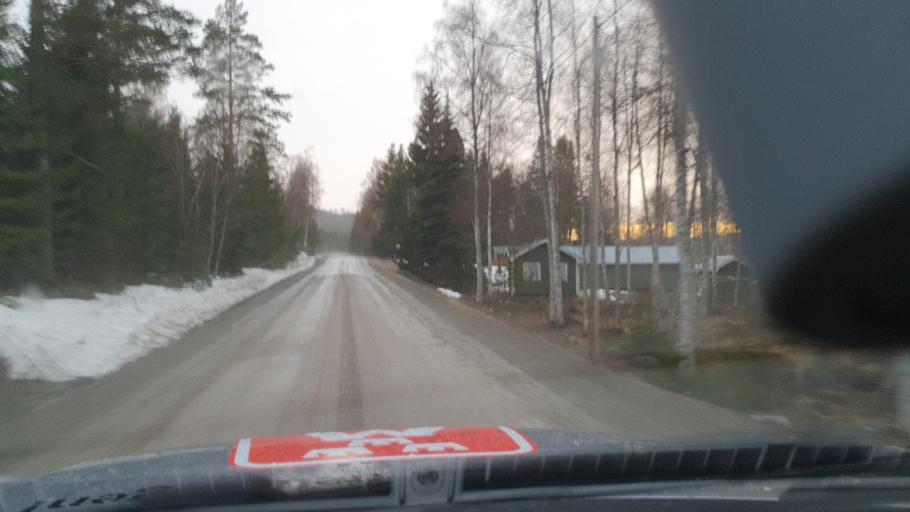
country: SE
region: Vaesternorrland
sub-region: OErnskoeldsviks Kommun
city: Bjasta
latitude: 63.2082
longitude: 18.3230
